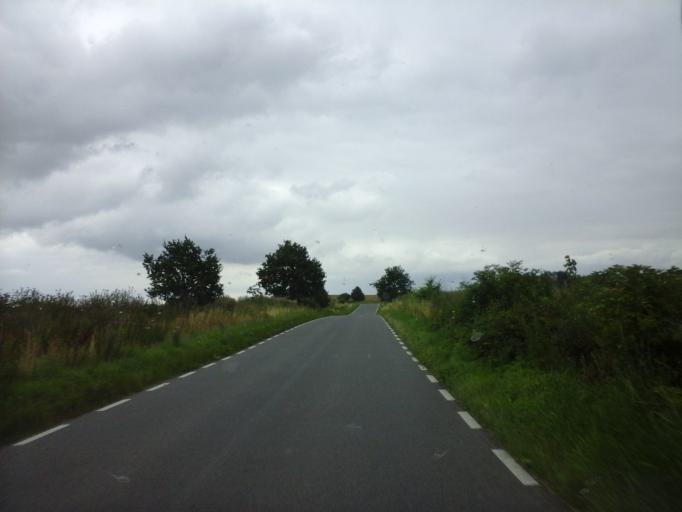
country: PL
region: West Pomeranian Voivodeship
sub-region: Powiat choszczenski
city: Pelczyce
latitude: 53.0068
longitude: 15.3979
